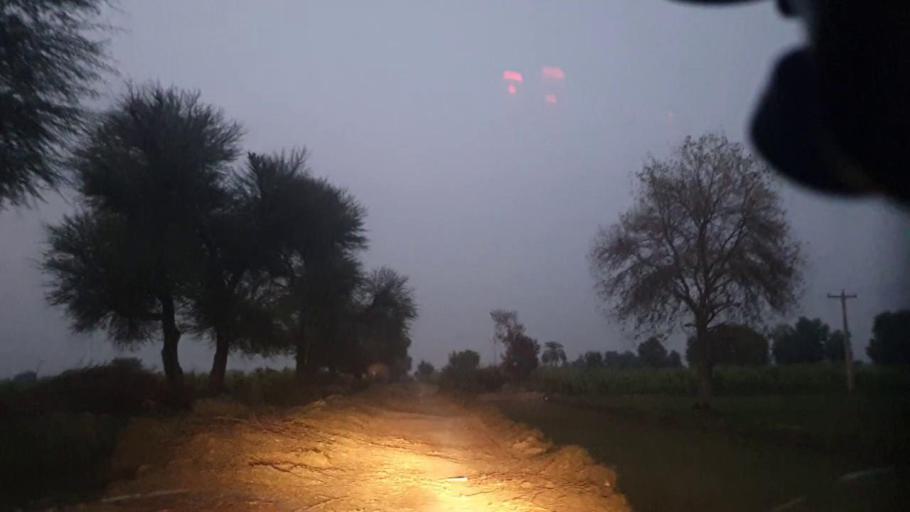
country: PK
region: Sindh
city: Hingorja
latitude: 27.2049
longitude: 68.3715
